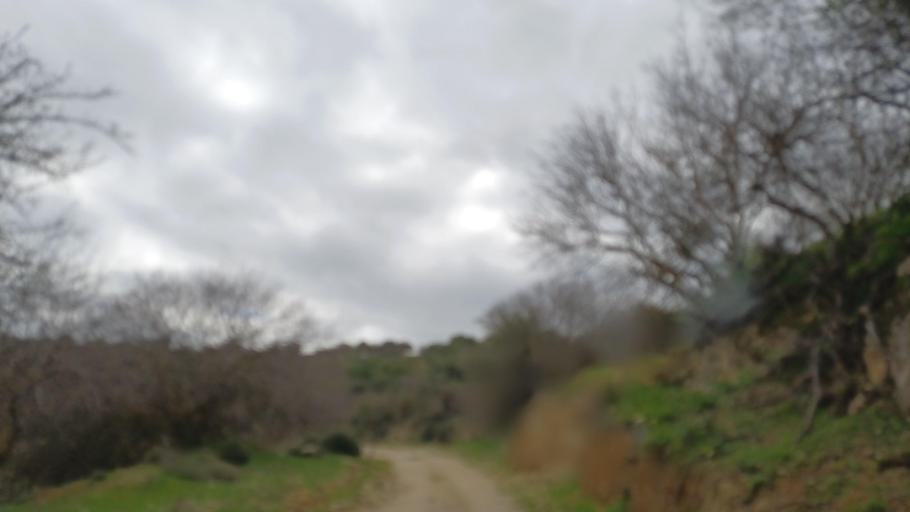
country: CY
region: Limassol
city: Pissouri
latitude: 34.7657
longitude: 32.6770
